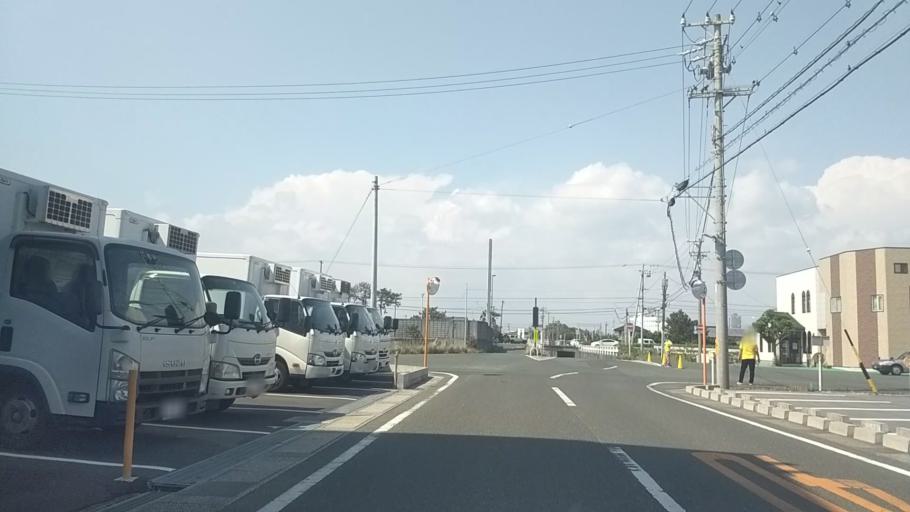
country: JP
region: Shizuoka
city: Hamamatsu
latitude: 34.6689
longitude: 137.7225
